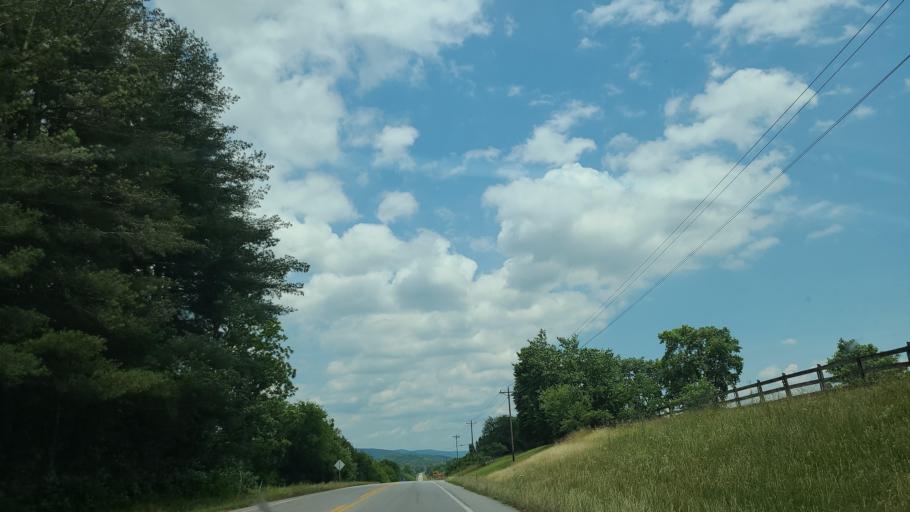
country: US
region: Tennessee
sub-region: Bledsoe County
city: Pikeville
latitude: 35.6294
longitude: -85.1774
